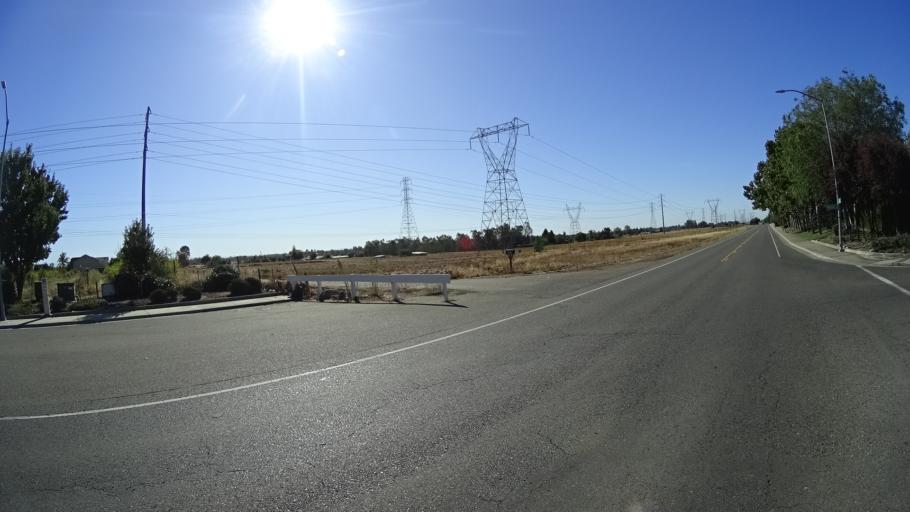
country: US
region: California
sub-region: Sacramento County
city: Vineyard
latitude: 38.4492
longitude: -121.3534
